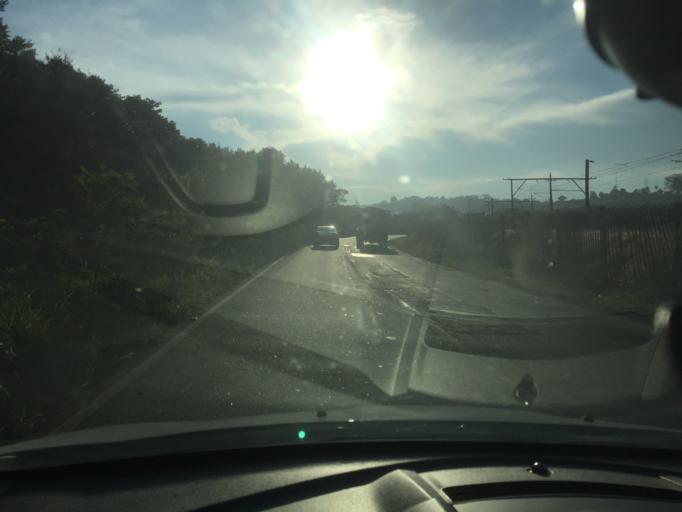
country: BR
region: Sao Paulo
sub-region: Varzea Paulista
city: Varzea Paulista
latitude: -23.2013
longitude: -46.8189
